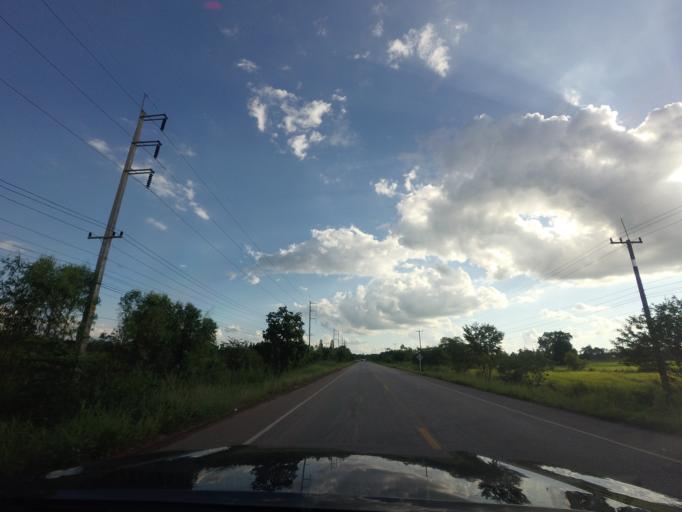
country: TH
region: Changwat Udon Thani
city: Thung Fon
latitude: 17.4665
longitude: 103.1918
